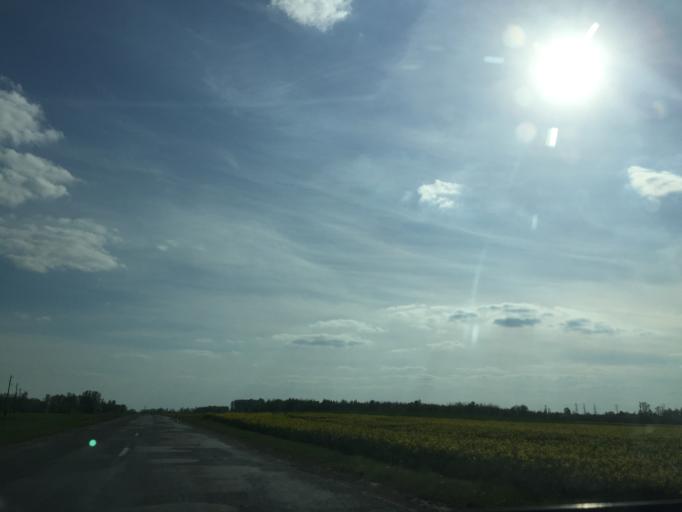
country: LV
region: Bauskas Rajons
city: Bauska
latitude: 56.4749
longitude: 24.3012
